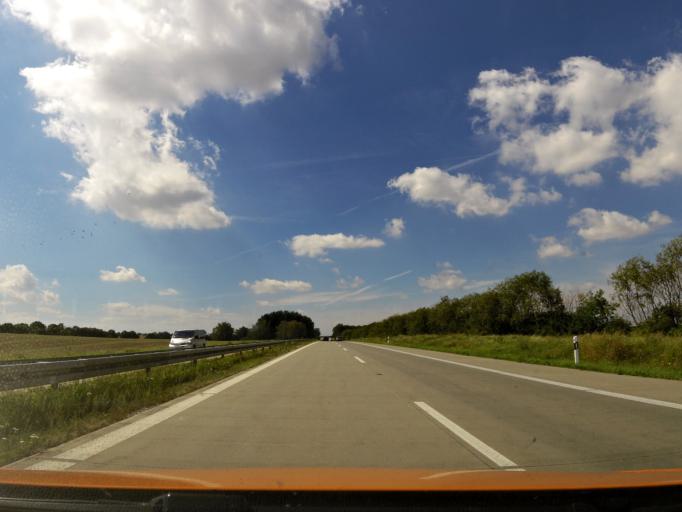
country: DE
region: Mecklenburg-Vorpommern
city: Penkun
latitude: 53.3029
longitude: 14.1938
